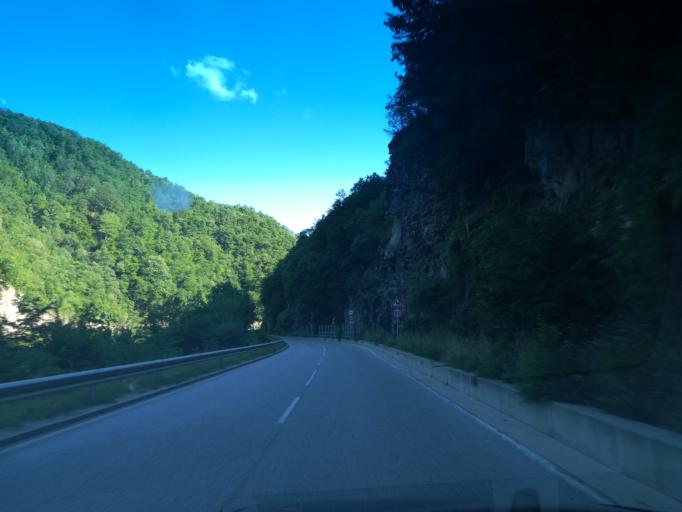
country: BG
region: Smolyan
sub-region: Obshtina Chepelare
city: Chepelare
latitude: 41.8008
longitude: 24.7097
